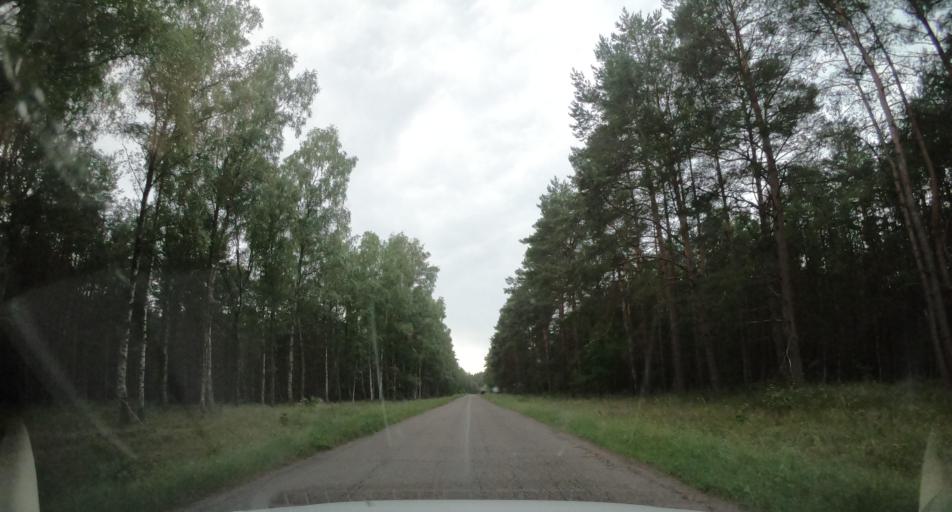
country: PL
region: West Pomeranian Voivodeship
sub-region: Powiat stargardzki
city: Insko
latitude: 53.4323
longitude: 15.6310
